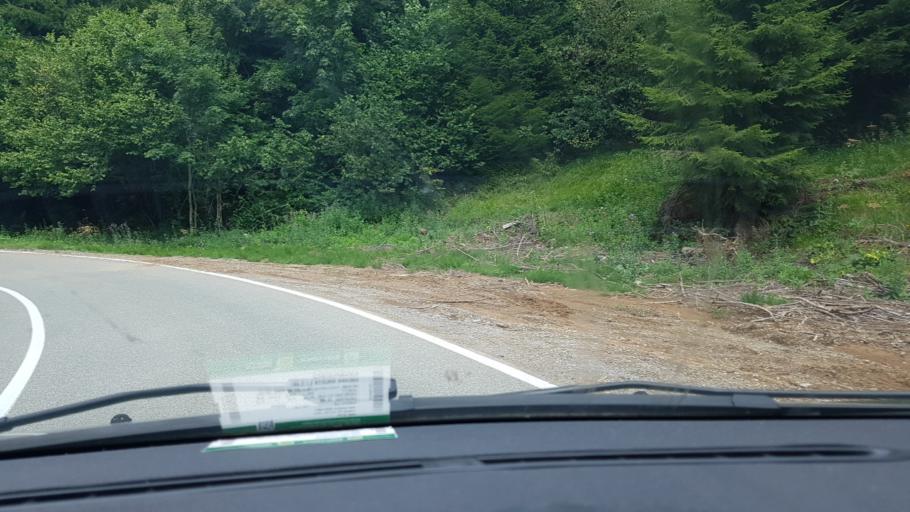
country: HR
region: Primorsko-Goranska
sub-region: Grad Delnice
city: Delnice
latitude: 45.3480
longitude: 14.7603
